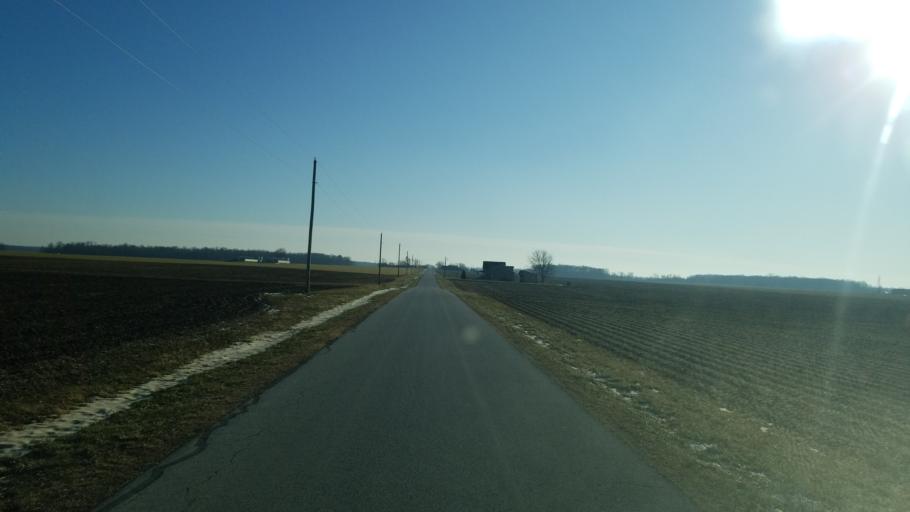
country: US
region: Ohio
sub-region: Sandusky County
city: Green Springs
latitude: 41.1923
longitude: -82.9953
